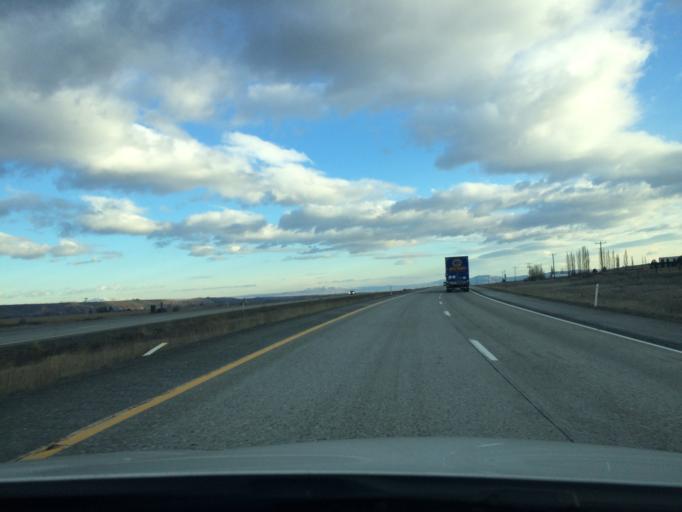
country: US
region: Washington
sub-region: Kittitas County
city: Ellensburg
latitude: 47.0786
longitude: -120.7233
